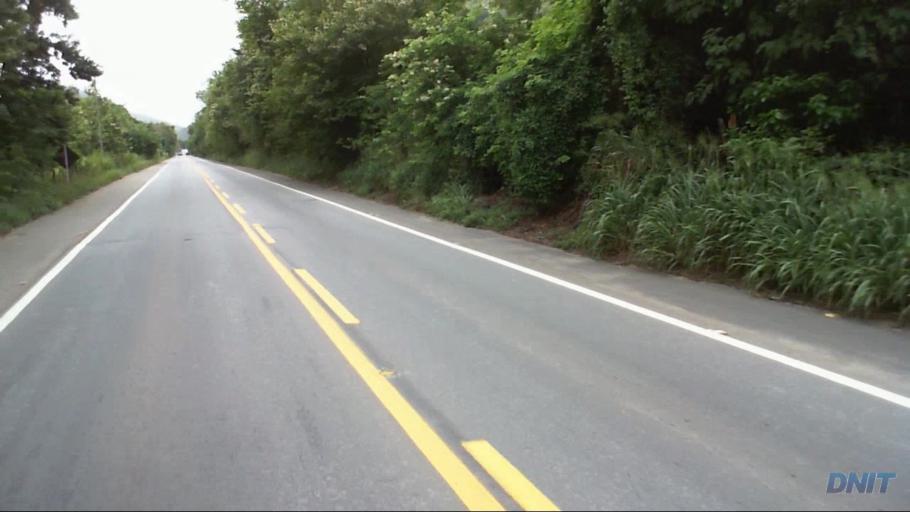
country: BR
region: Minas Gerais
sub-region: Timoteo
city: Timoteo
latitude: -19.5532
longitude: -42.7080
